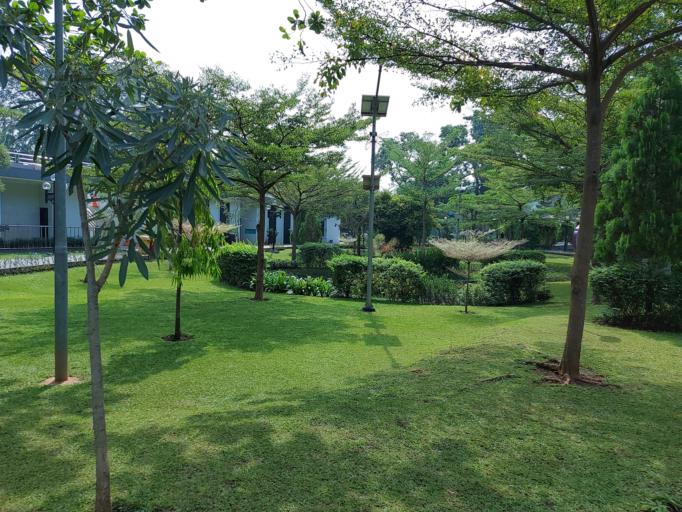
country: ID
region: West Java
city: Cibinong
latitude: -6.4807
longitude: 106.8259
